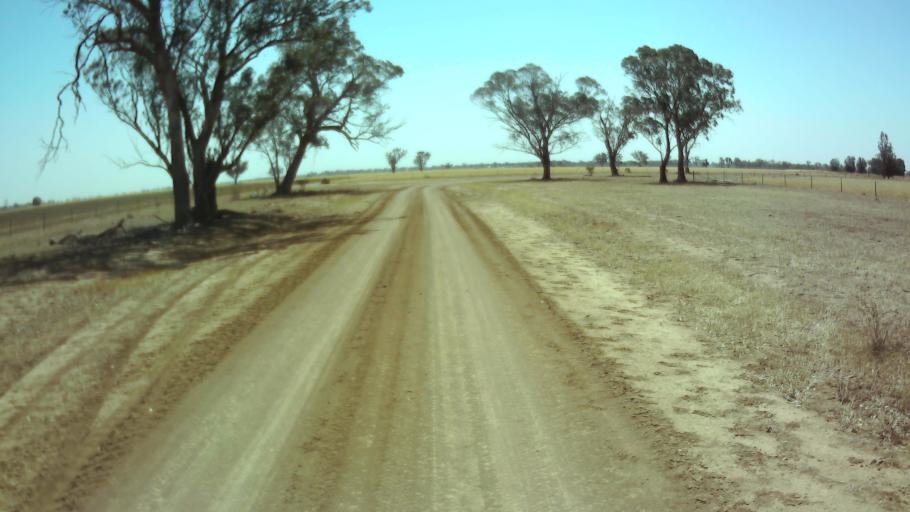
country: AU
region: New South Wales
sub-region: Weddin
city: Grenfell
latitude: -34.0023
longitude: 147.8774
